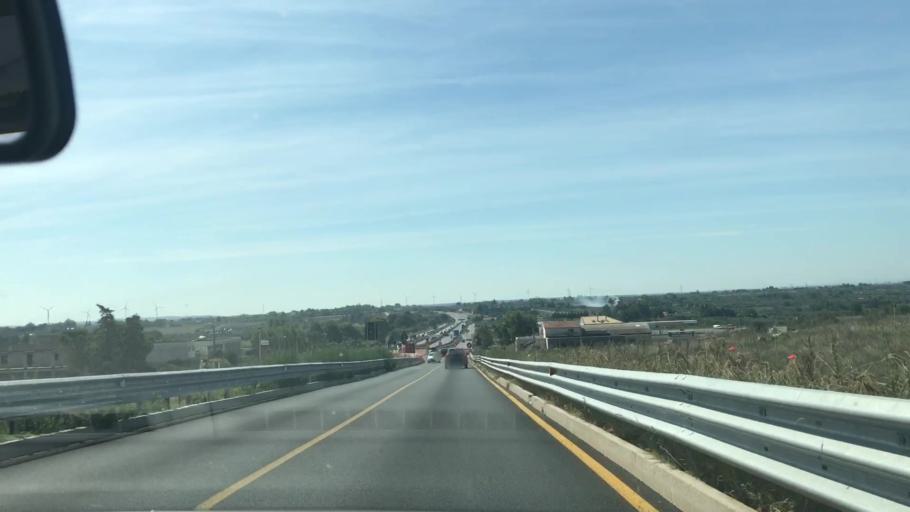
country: IT
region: Apulia
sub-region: Provincia di Bari
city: Altamura
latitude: 40.8080
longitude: 16.5556
